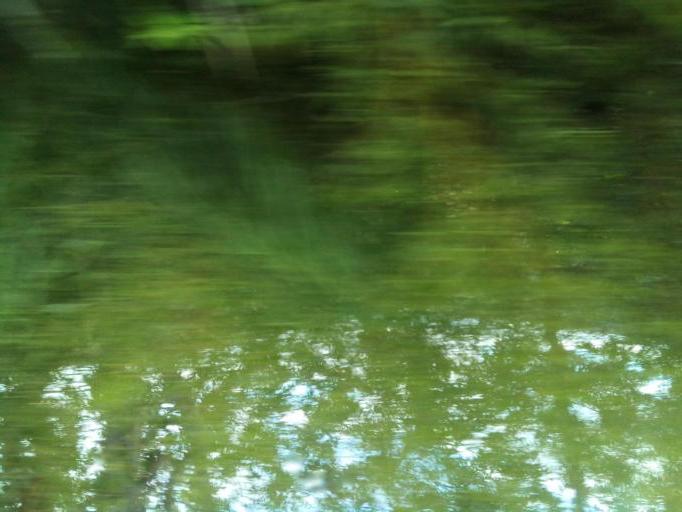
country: BR
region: Minas Gerais
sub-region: Santa Luzia
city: Santa Luzia
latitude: -19.8690
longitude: -43.8405
